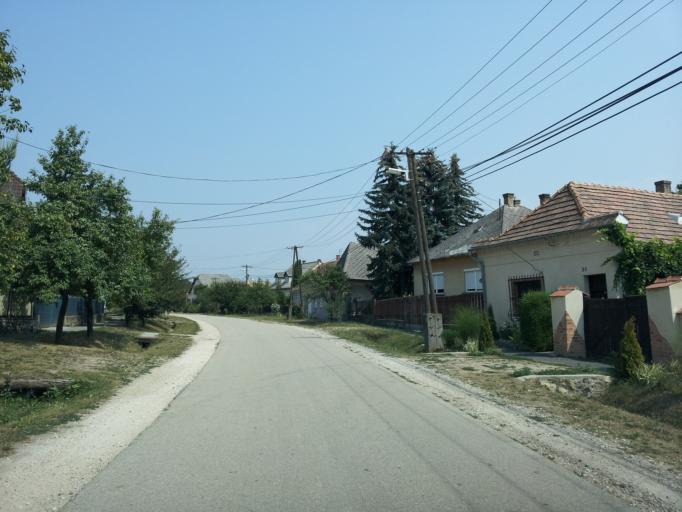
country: HU
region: Gyor-Moson-Sopron
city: Bakonyszentlaszlo
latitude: 47.4646
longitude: 17.7968
